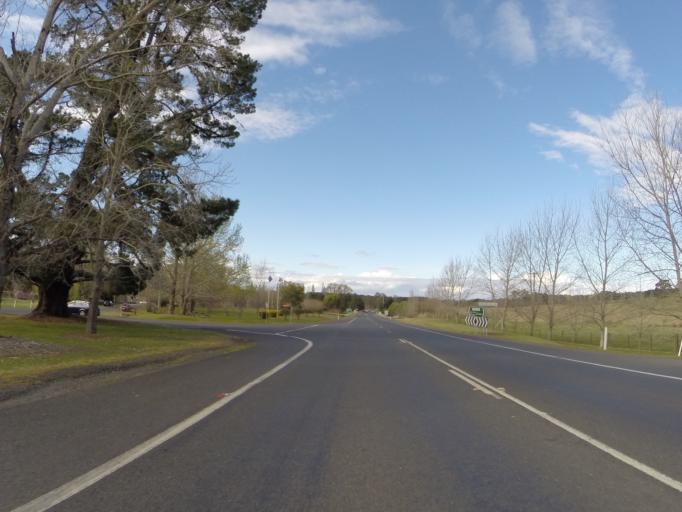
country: AU
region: New South Wales
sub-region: Wingecarribee
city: Moss Vale
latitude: -34.5678
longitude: 150.3216
